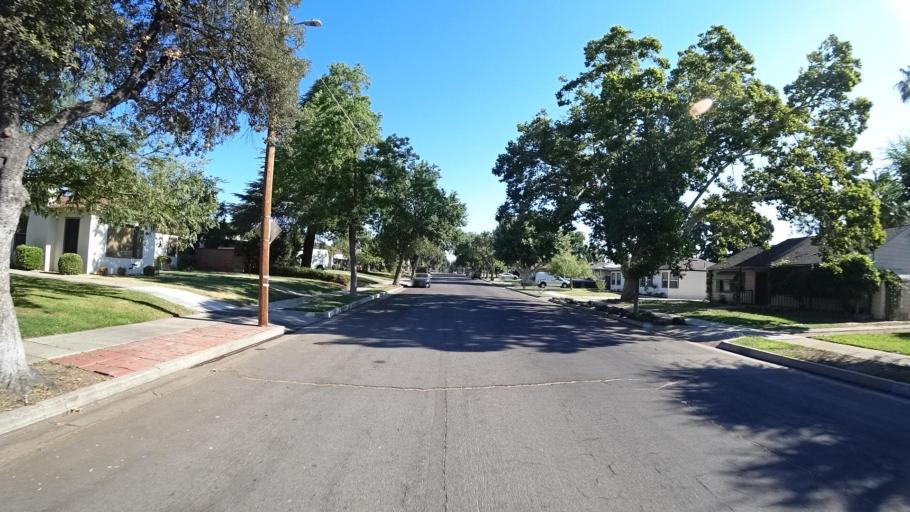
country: US
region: California
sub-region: Fresno County
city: Fresno
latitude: 36.7637
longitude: -119.8132
